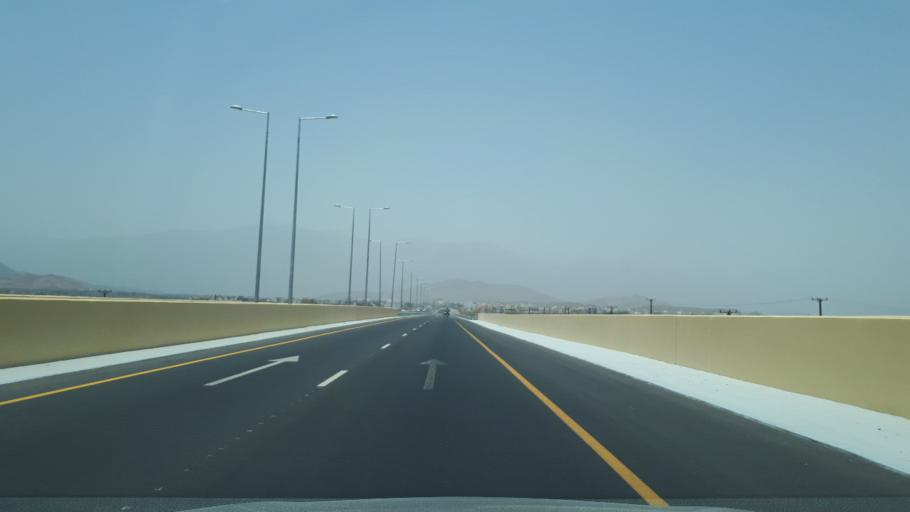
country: OM
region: Al Batinah
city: Rustaq
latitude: 23.4679
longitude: 57.4426
